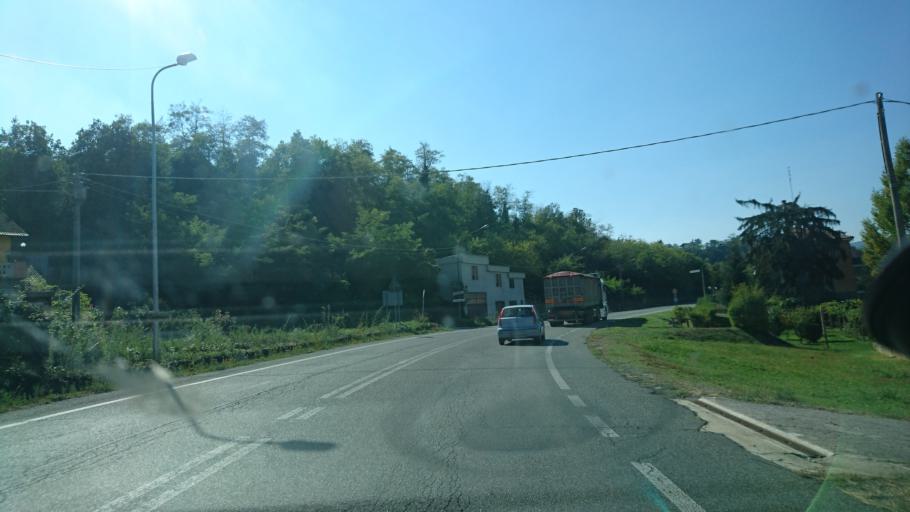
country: IT
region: Piedmont
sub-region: Provincia di Alessandria
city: Spigno Monferrato
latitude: 44.5433
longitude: 8.3383
